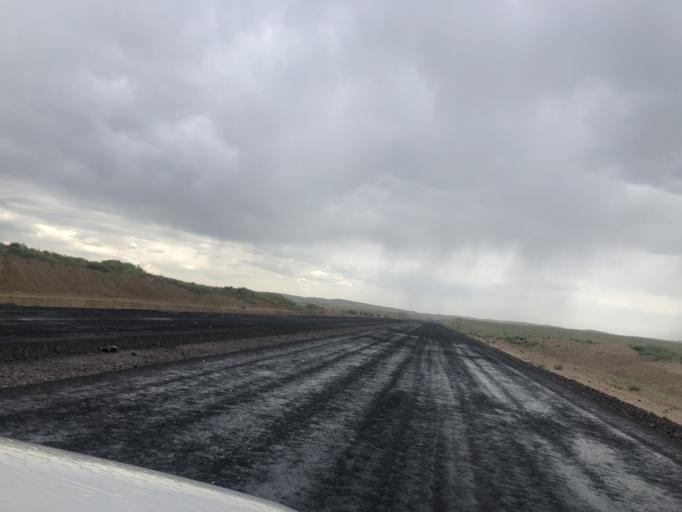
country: KG
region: Chuy
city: Bystrovka
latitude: 43.3206
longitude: 75.8900
